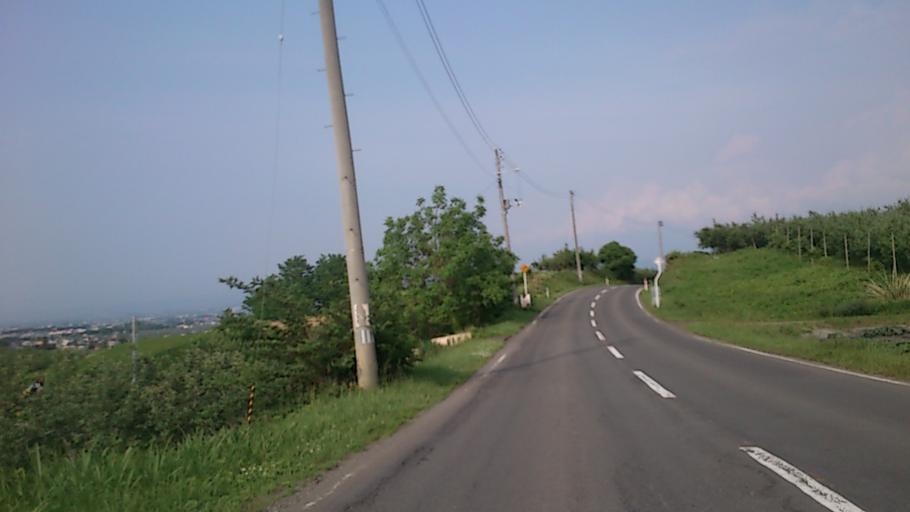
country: JP
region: Aomori
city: Hirosaki
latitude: 40.5587
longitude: 140.4782
